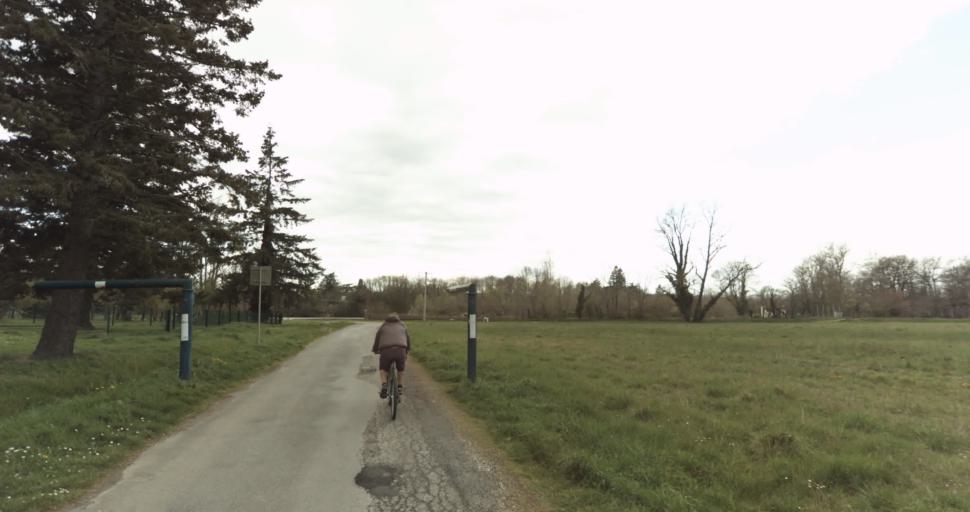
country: FR
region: Midi-Pyrenees
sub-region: Departement de la Haute-Garonne
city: Auterive
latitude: 43.3405
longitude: 1.4835
